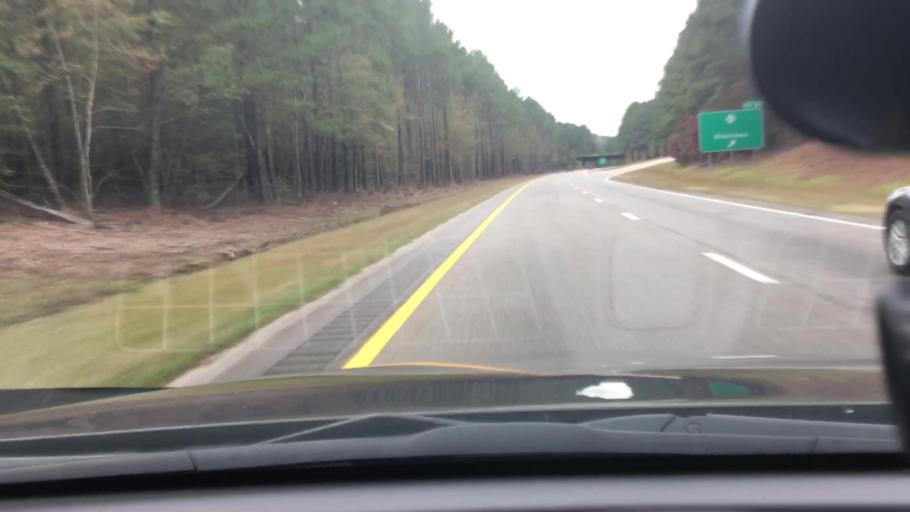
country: US
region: North Carolina
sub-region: Wake County
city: Zebulon
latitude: 35.7987
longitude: -78.1841
